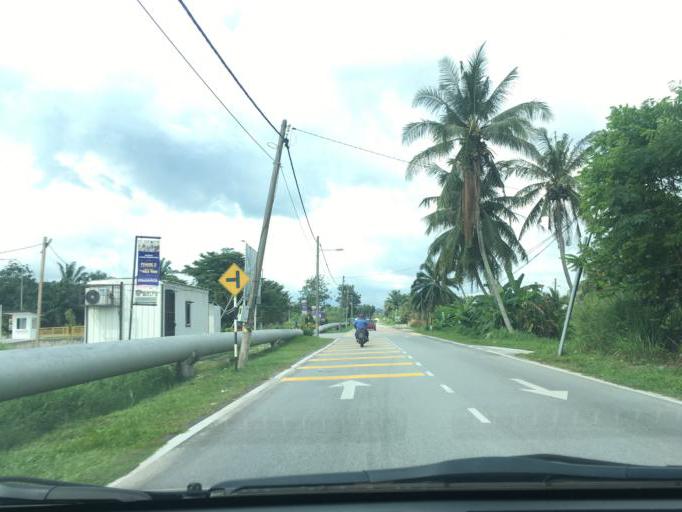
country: MY
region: Selangor
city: Kampung Baru Subang
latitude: 3.1433
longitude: 101.4488
